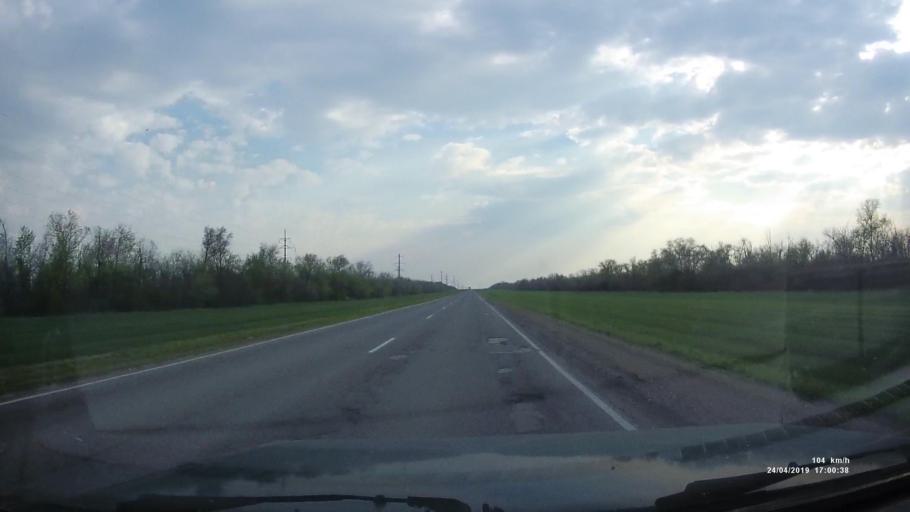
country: RU
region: Rostov
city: Proletarsk
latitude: 46.6029
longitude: 41.6361
